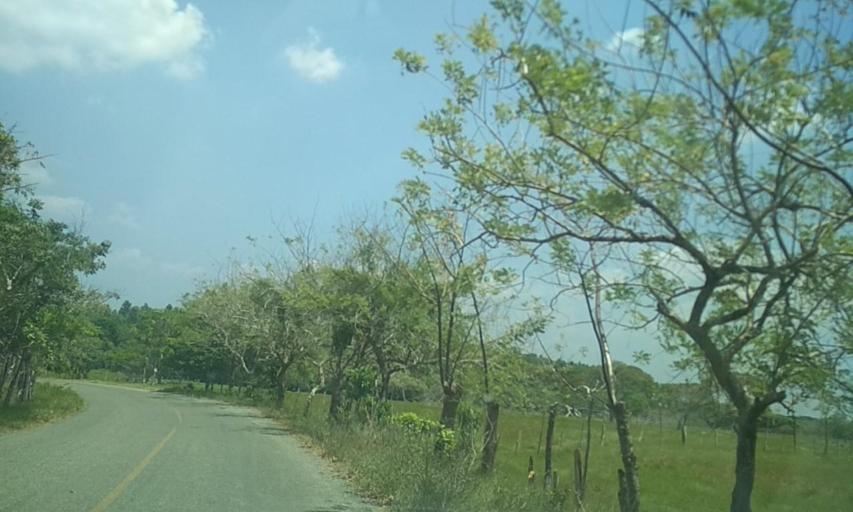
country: MX
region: Tabasco
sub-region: Huimanguillo
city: Francisco Rueda
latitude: 17.8356
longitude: -93.9164
